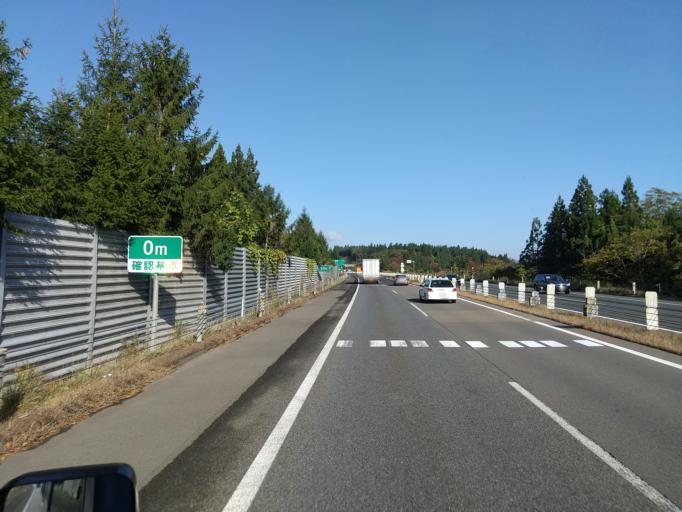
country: JP
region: Iwate
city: Hanamaki
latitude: 39.4877
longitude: 141.1101
